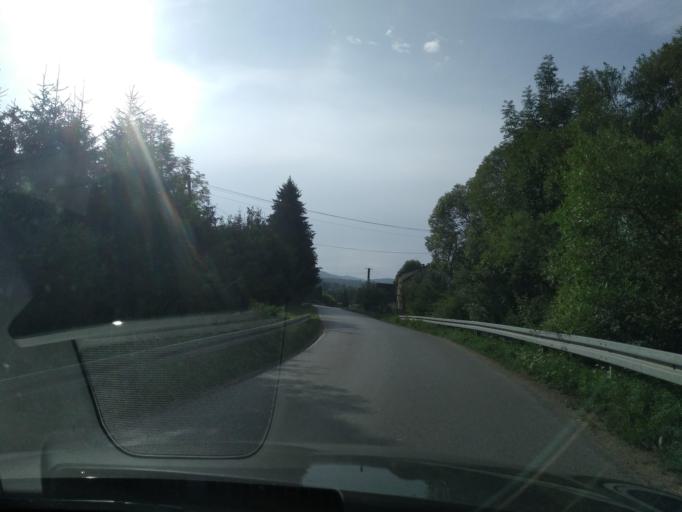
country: PL
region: Subcarpathian Voivodeship
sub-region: Powiat sanocki
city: Tyrawa Woloska
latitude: 49.5406
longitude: 22.4093
